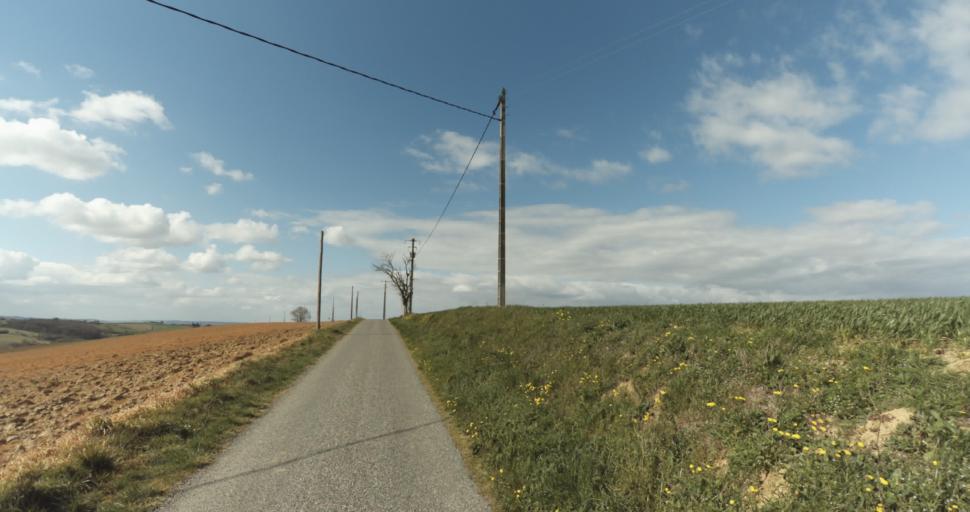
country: FR
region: Midi-Pyrenees
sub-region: Departement de la Haute-Garonne
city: Auterive
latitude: 43.3633
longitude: 1.5109
